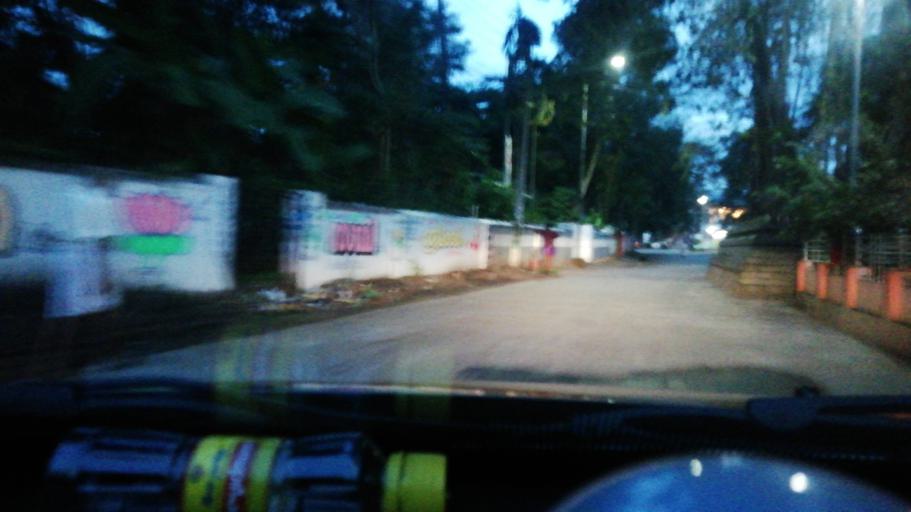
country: IN
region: Kerala
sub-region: Thiruvananthapuram
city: Paravur
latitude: 8.8123
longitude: 76.6676
